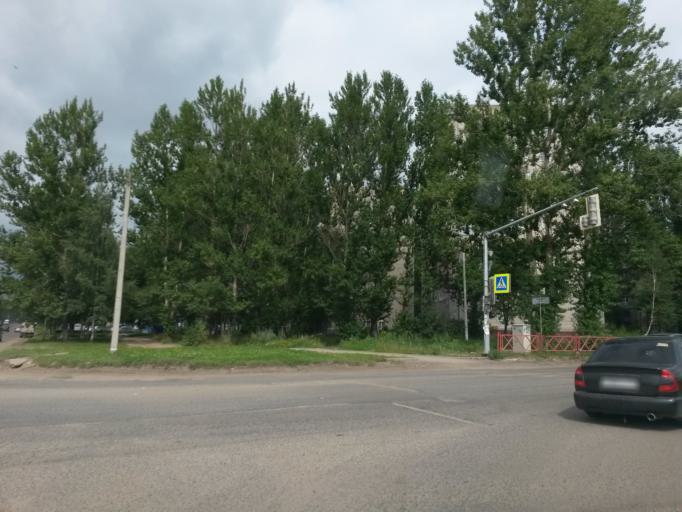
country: RU
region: Jaroslavl
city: Yaroslavl
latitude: 57.5707
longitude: 39.8588
